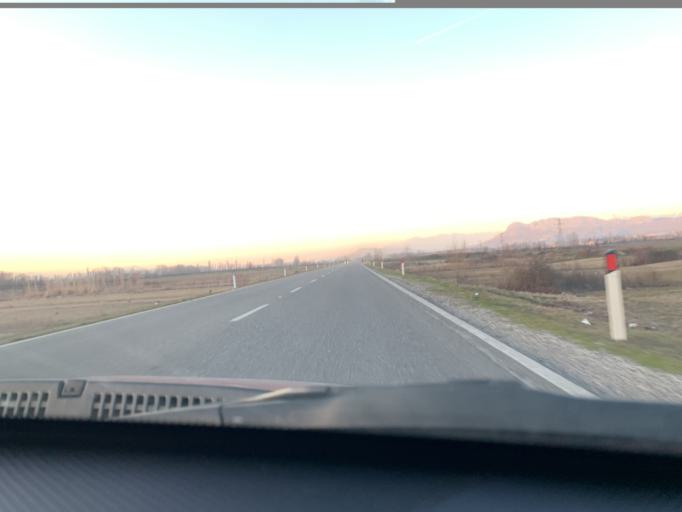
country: AL
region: Lezhe
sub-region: Rrethi i Lezhes
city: Balldreni i Ri
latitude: 41.8449
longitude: 19.6431
